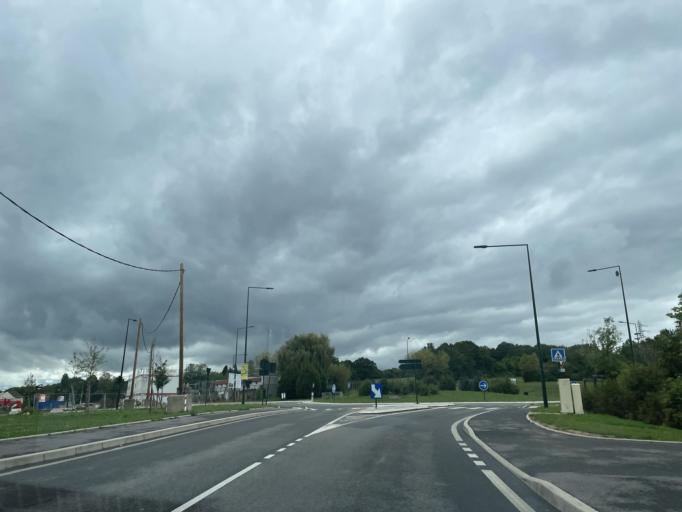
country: FR
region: Ile-de-France
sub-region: Departement de Seine-et-Marne
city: Coulommiers
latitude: 48.8149
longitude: 3.1082
